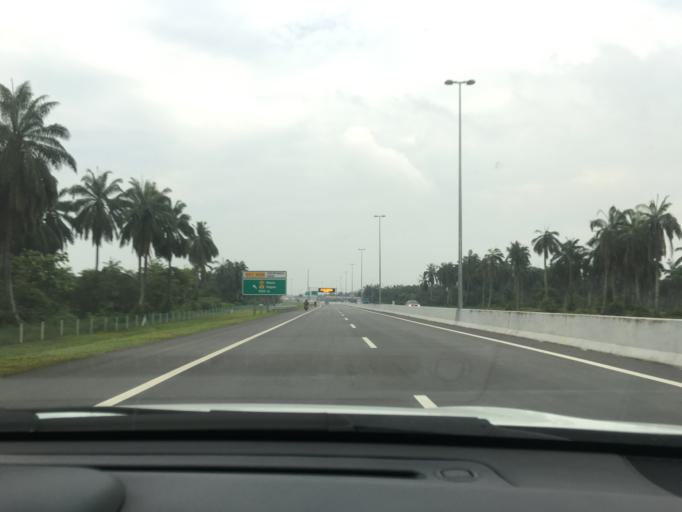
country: MY
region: Selangor
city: Klang
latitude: 3.1229
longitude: 101.4074
